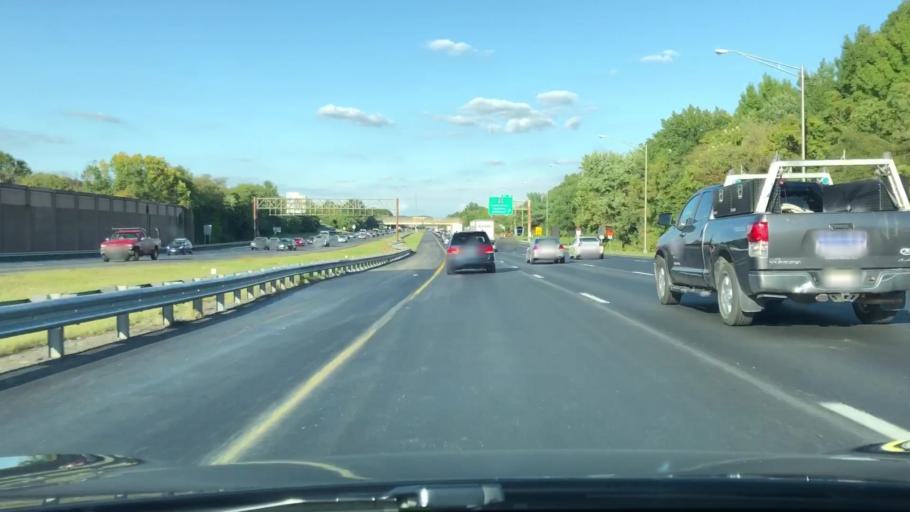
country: US
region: New Jersey
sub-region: Camden County
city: Ashland
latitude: 39.8772
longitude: -75.0134
